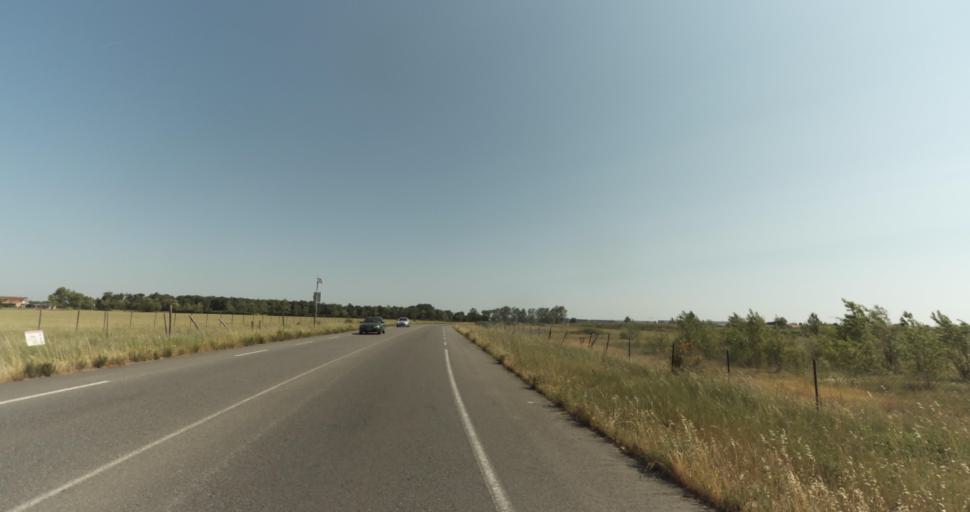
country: FR
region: Midi-Pyrenees
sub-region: Departement de la Haute-Garonne
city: La Salvetat-Saint-Gilles
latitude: 43.5888
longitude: 1.2808
